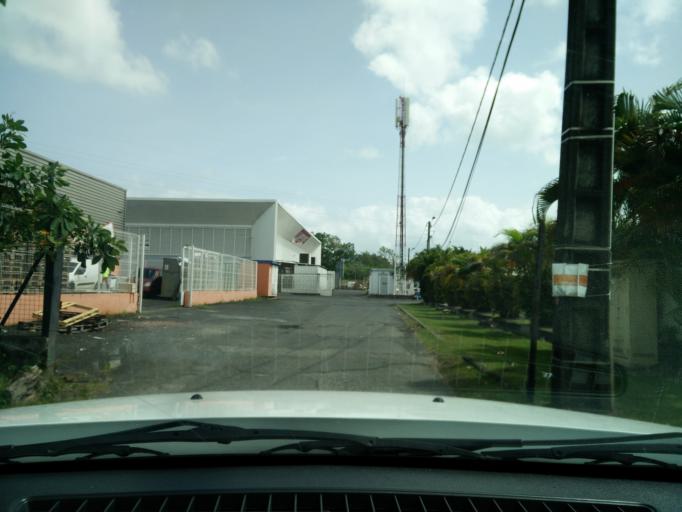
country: GP
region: Guadeloupe
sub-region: Guadeloupe
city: Pointe-a-Pitre
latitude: 16.2531
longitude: -61.5534
